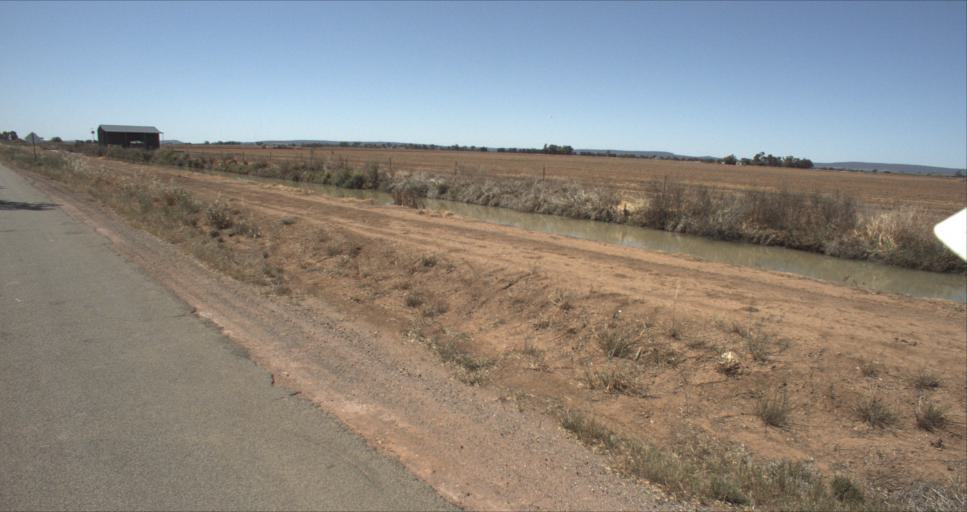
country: AU
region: New South Wales
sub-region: Leeton
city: Leeton
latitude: -34.5234
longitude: 146.3458
